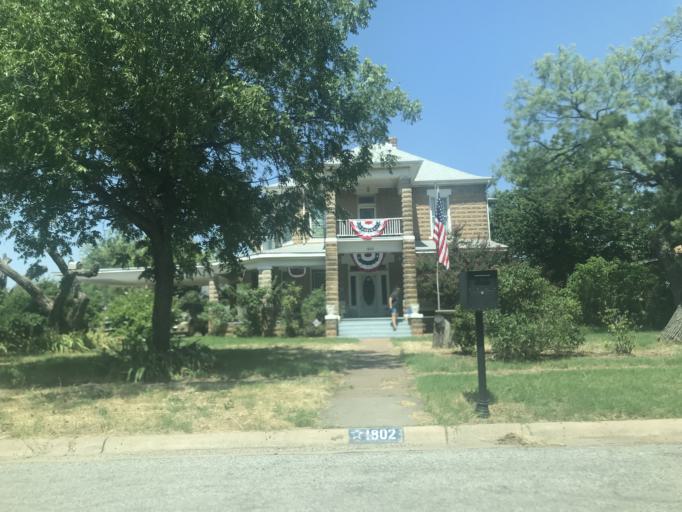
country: US
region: Texas
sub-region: Taylor County
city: Abilene
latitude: 32.4700
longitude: -99.7409
